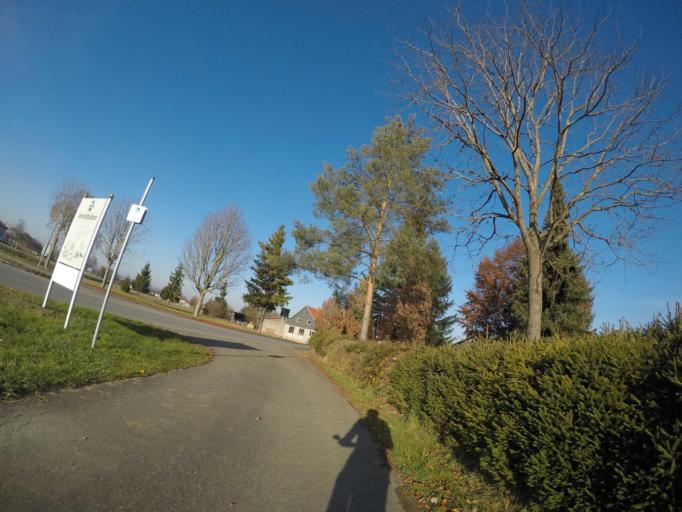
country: DE
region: Baden-Wuerttemberg
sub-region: Tuebingen Region
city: Unterstadion
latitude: 48.2004
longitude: 9.6846
